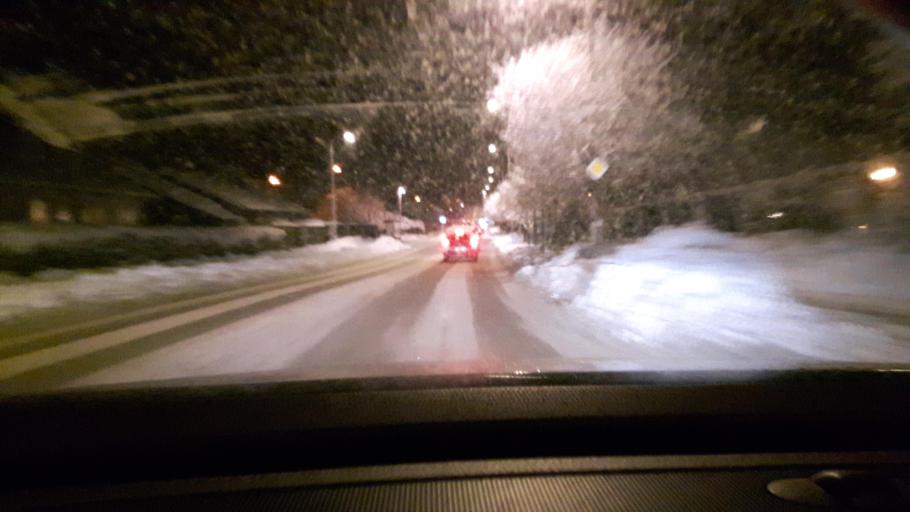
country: SE
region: Vaestra Goetaland
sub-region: Goteborg
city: Majorna
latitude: 57.6628
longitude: 11.8783
